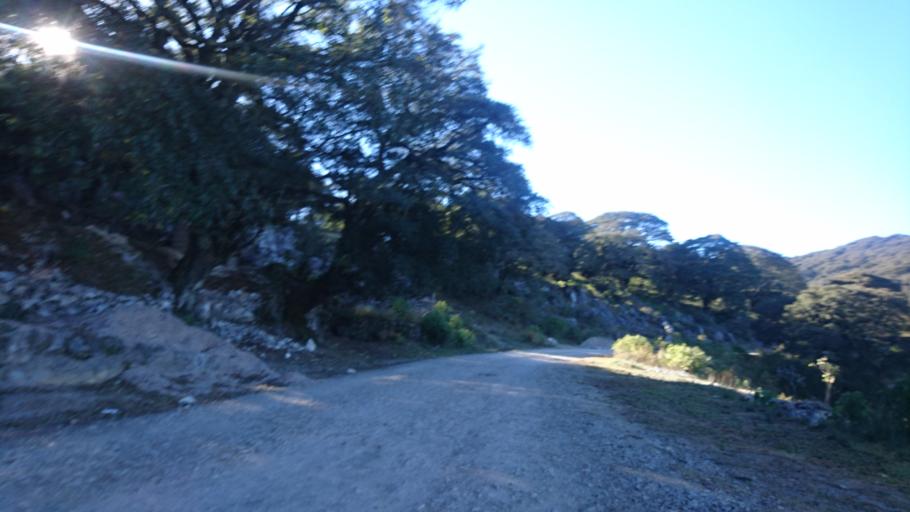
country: MX
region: San Luis Potosi
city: Zaragoza
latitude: 22.0305
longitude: -100.6086
